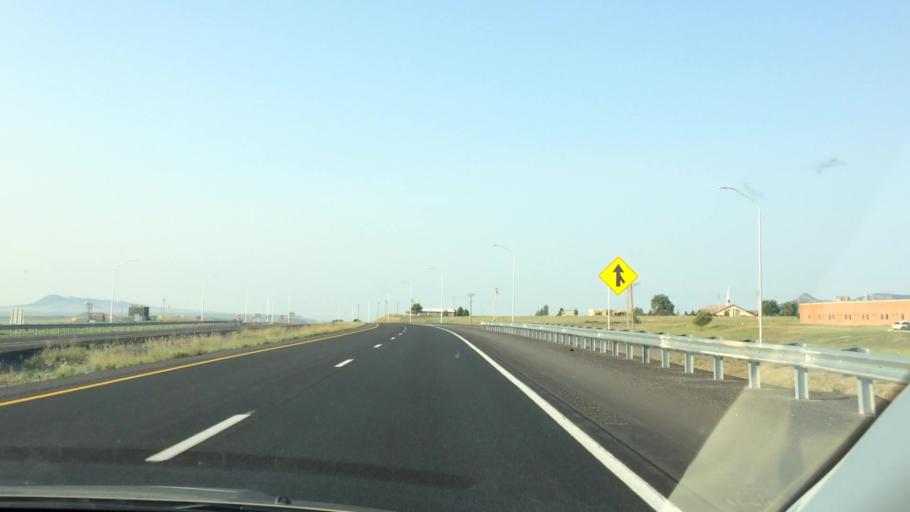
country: US
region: New Mexico
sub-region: Colfax County
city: Raton
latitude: 36.8639
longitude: -104.4397
